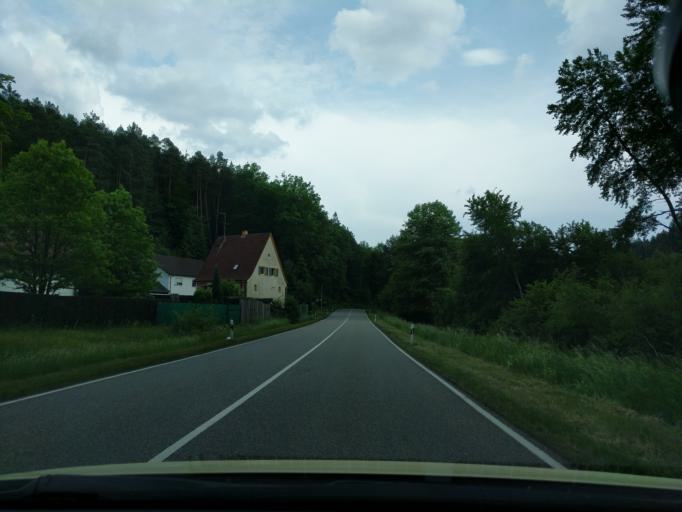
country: DE
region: Rheinland-Pfalz
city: Stelzenberg
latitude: 49.3874
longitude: 7.7002
